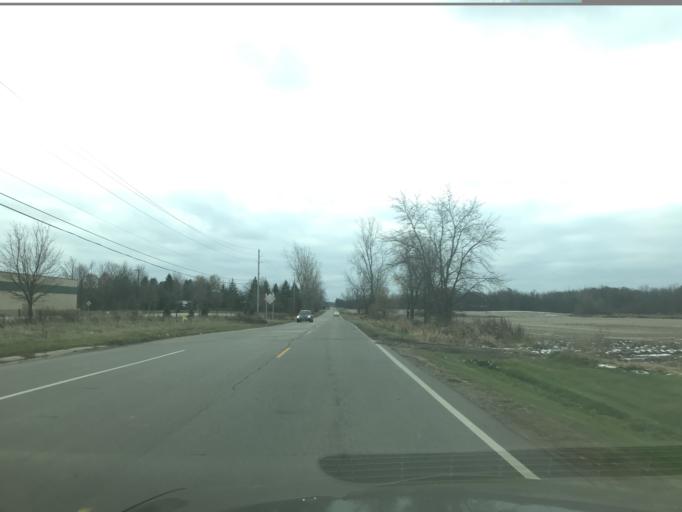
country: US
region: Michigan
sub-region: Eaton County
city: Waverly
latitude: 42.7398
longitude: -84.6816
